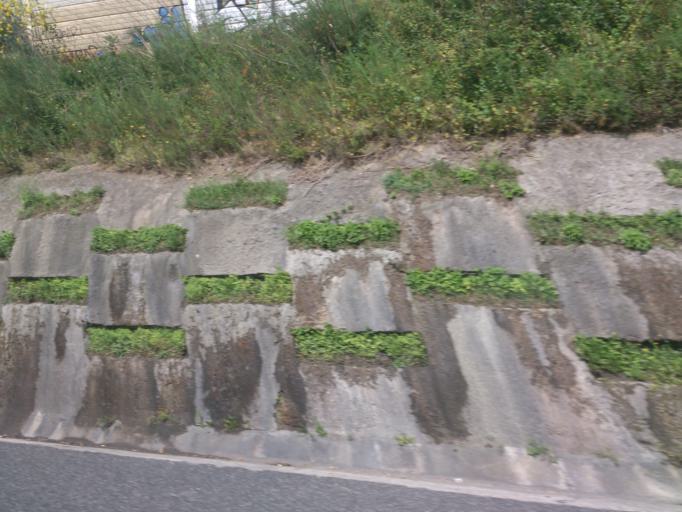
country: PT
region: Lisbon
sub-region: Loures
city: Sacavem
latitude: 38.7955
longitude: -9.1117
